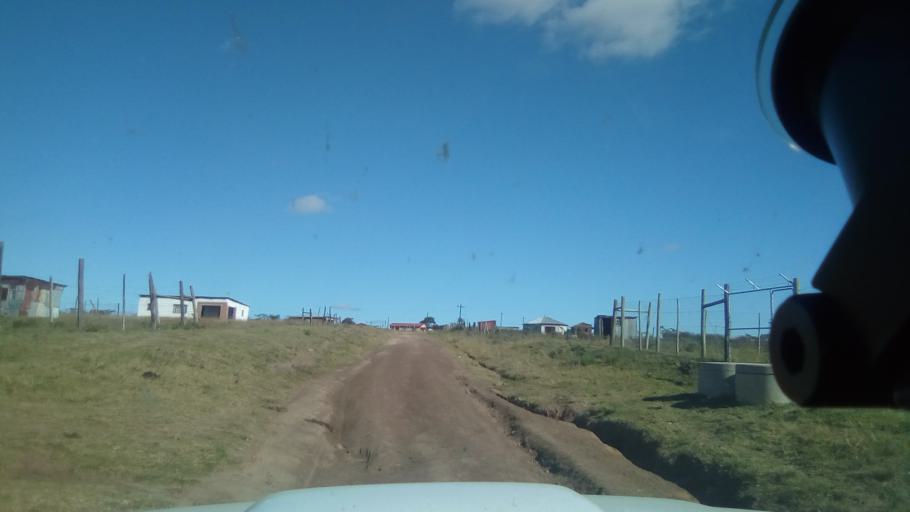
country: ZA
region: Eastern Cape
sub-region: Buffalo City Metropolitan Municipality
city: Bhisho
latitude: -32.7803
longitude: 27.3377
